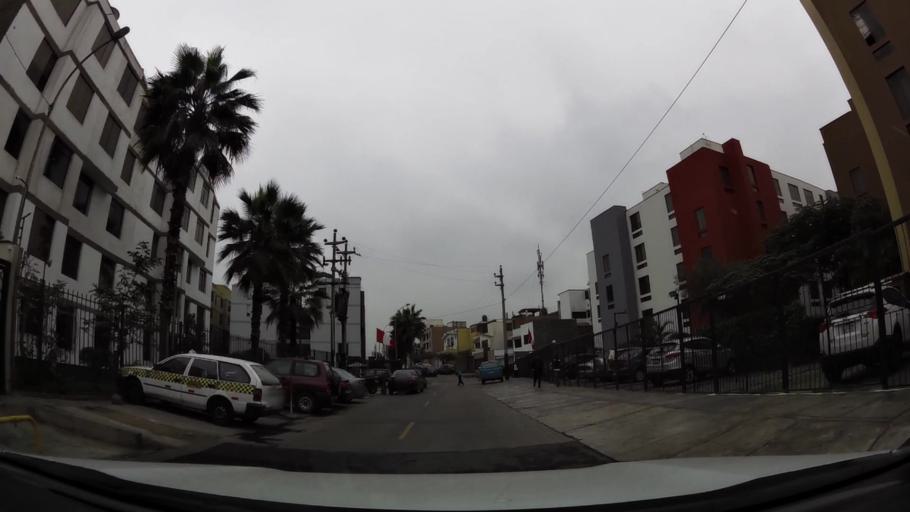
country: PE
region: Lima
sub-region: Lima
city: Surco
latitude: -12.1345
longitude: -77.0059
